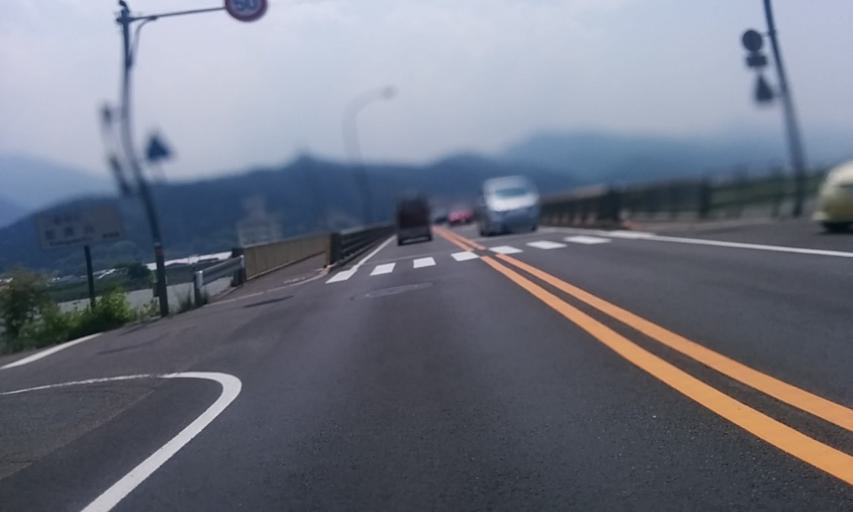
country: JP
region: Ehime
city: Saijo
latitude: 33.9047
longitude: 133.1852
